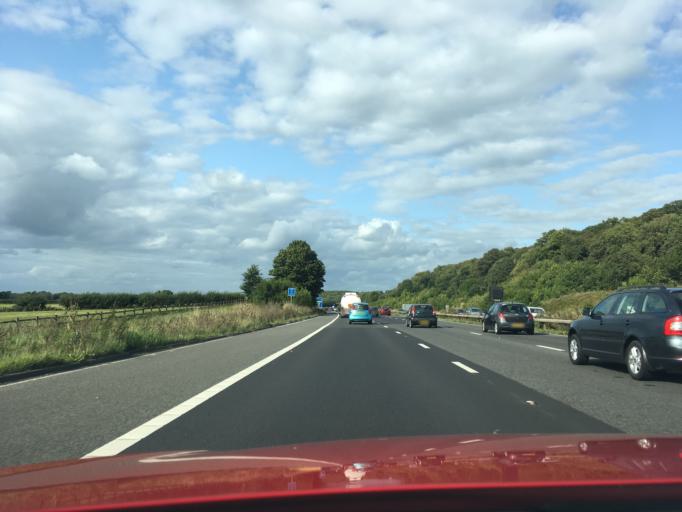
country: GB
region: England
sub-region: South Gloucestershire
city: Falfield
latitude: 51.6439
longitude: -2.4443
